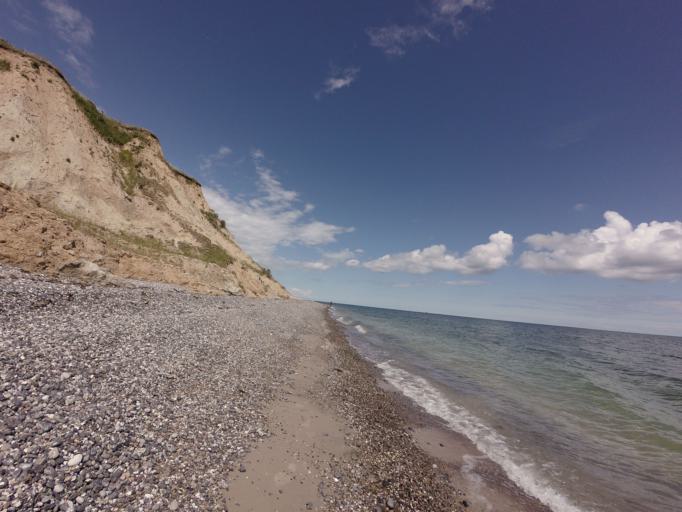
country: DK
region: Central Jutland
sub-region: Norddjurs Kommune
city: Grenaa
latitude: 56.5135
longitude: 10.8651
